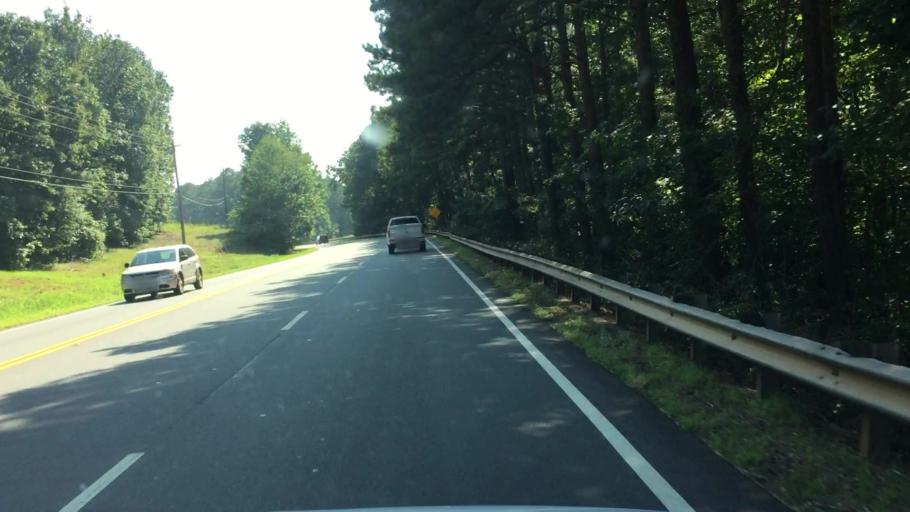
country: US
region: Georgia
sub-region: Gwinnett County
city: Dacula
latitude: 33.9993
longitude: -83.8757
